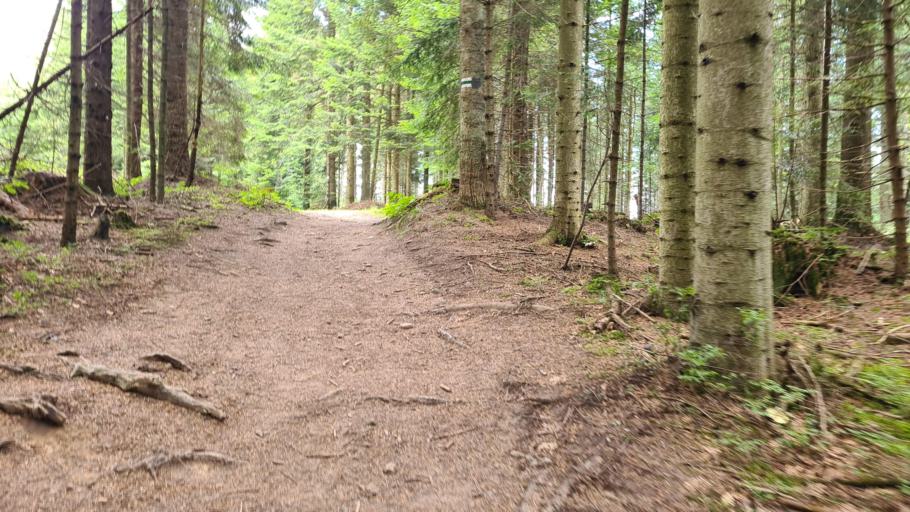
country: PL
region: Lesser Poland Voivodeship
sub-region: Powiat nowosadecki
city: Rytro
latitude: 49.4158
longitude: 20.6227
